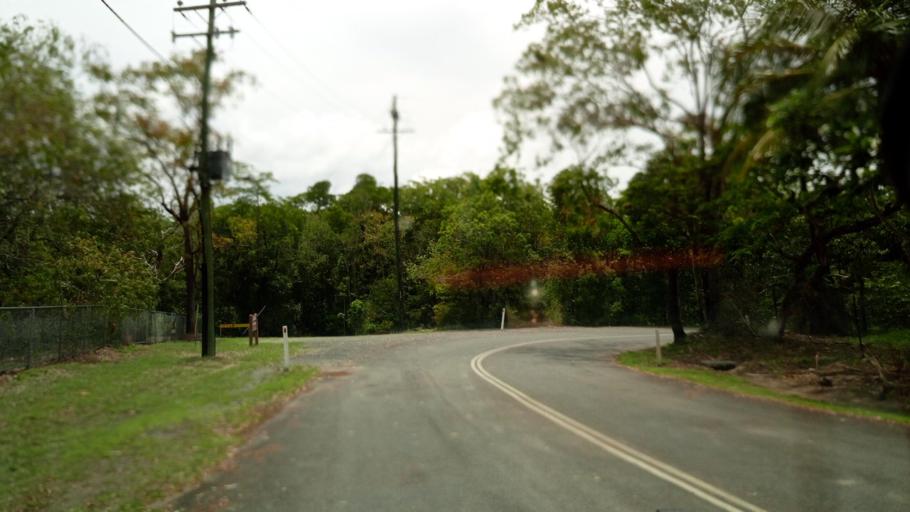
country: AU
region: Queensland
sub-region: Cairns
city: Redlynch
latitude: -16.8566
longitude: 145.7540
